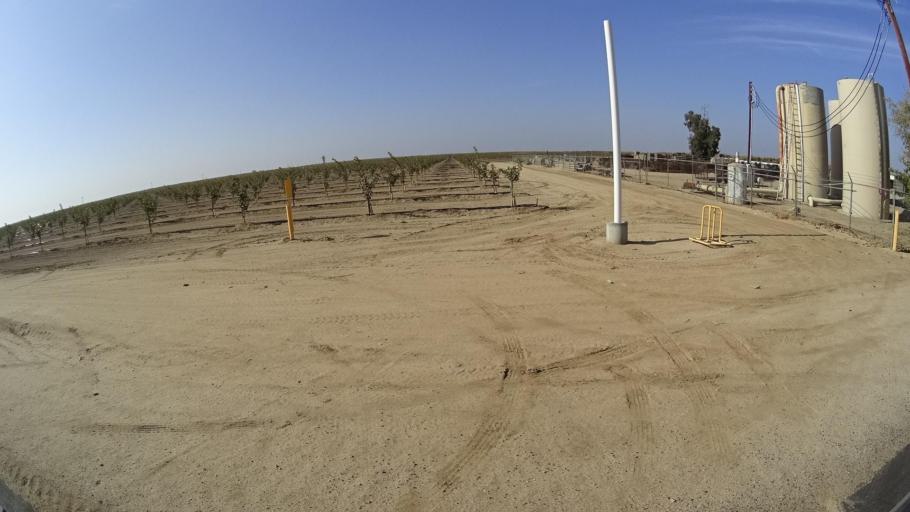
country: US
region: California
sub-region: Kern County
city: Shafter
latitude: 35.5467
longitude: -119.1511
